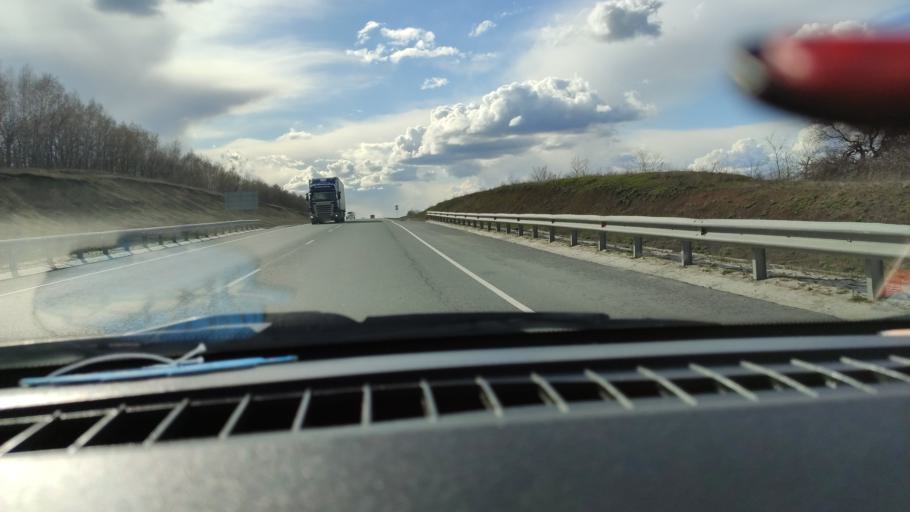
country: RU
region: Saratov
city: Shikhany
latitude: 52.1163
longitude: 47.2866
